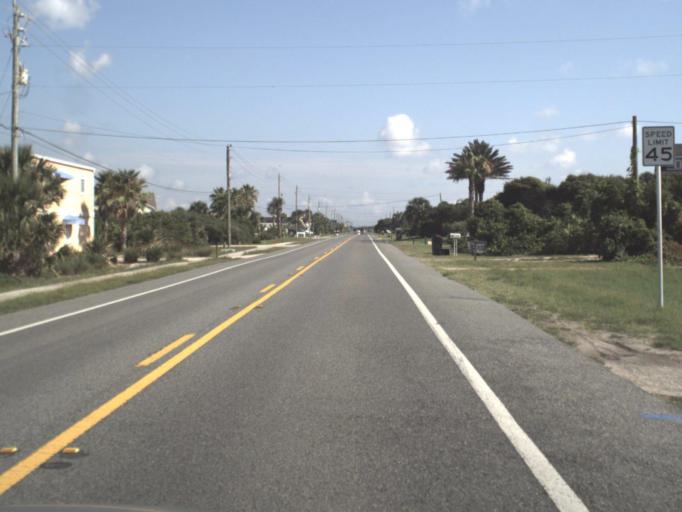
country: US
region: Florida
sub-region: Saint Johns County
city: Butler Beach
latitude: 29.7596
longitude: -81.2499
